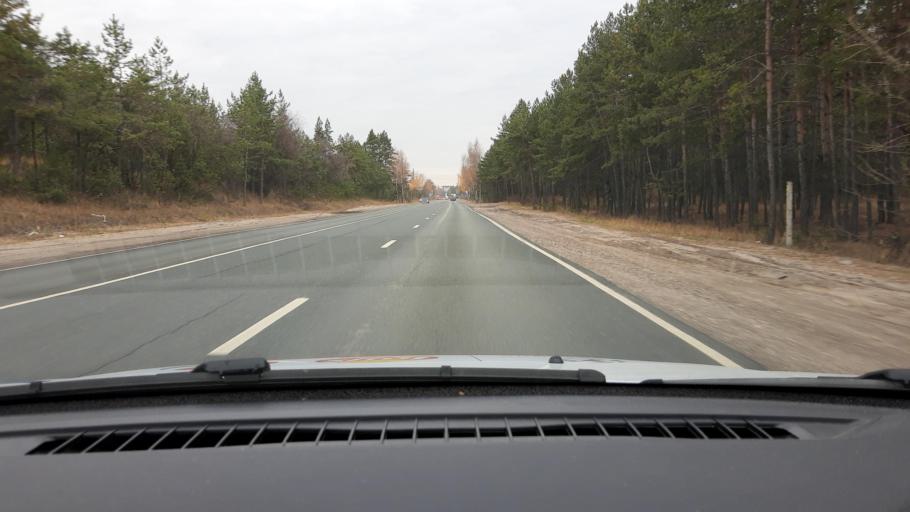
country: RU
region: Nizjnij Novgorod
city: Dzerzhinsk
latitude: 56.2717
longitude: 43.4734
